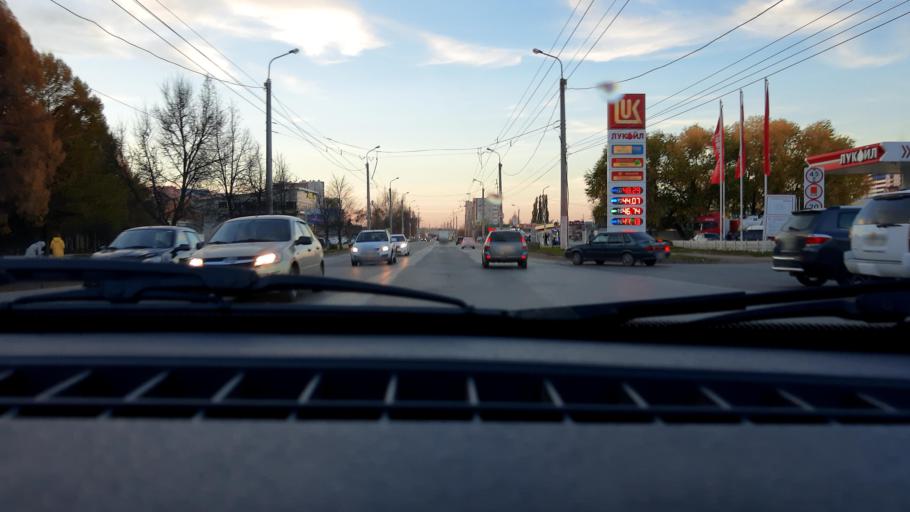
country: RU
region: Bashkortostan
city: Mikhaylovka
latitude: 54.7904
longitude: 55.8795
